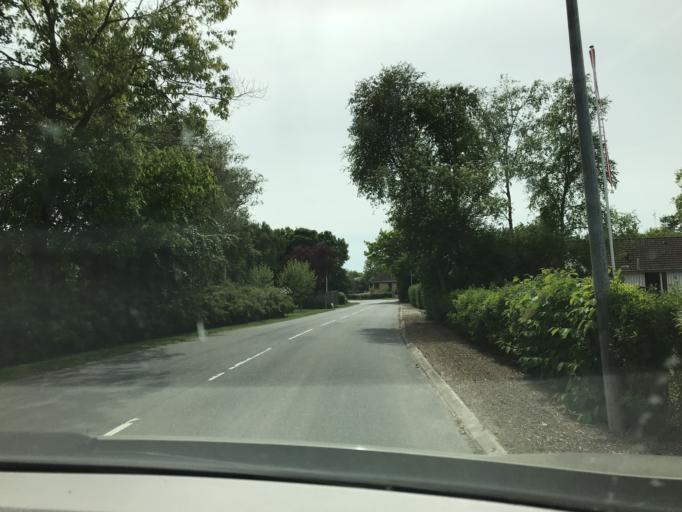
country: DK
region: Central Jutland
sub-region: Norddjurs Kommune
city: Allingabro
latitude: 56.5551
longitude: 10.3005
